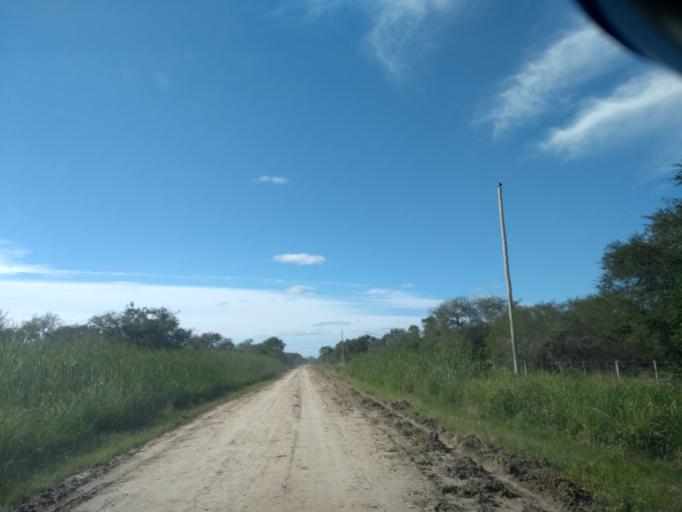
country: AR
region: Chaco
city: Colonia Benitez
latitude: -27.2867
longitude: -58.9309
